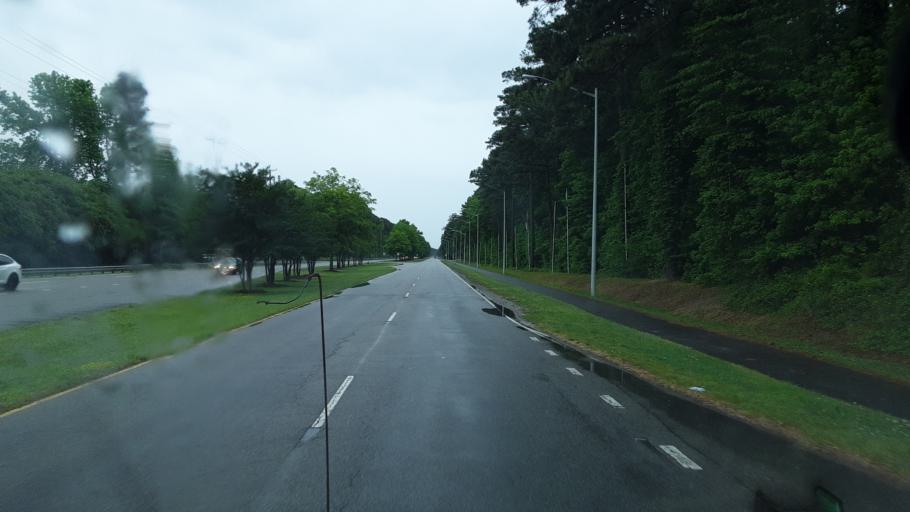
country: US
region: Virginia
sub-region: City of Virginia Beach
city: Virginia Beach
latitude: 36.8096
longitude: -75.9903
